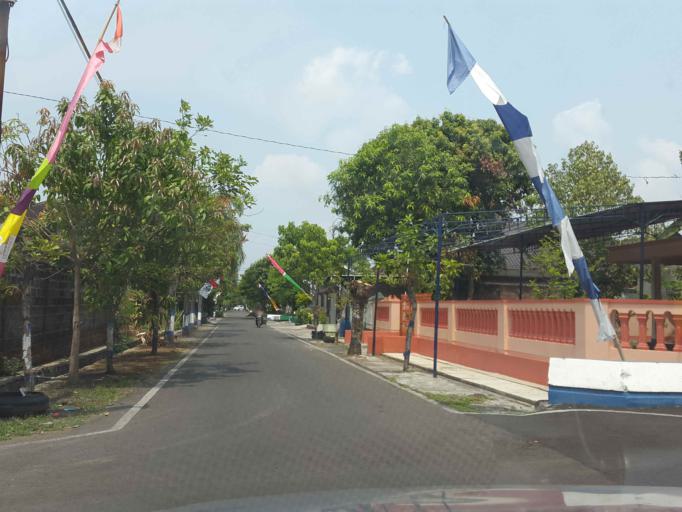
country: ID
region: Central Java
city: Jaten
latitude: -7.5920
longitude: 110.9382
